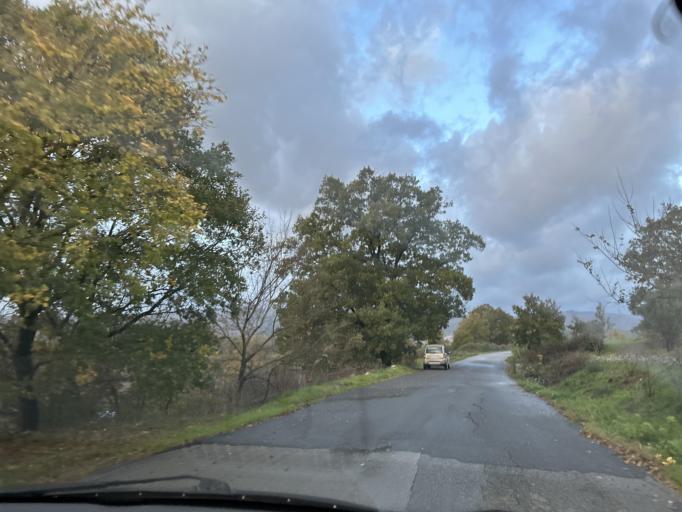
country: IT
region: Calabria
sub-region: Provincia di Catanzaro
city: Squillace
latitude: 38.7746
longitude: 16.4993
